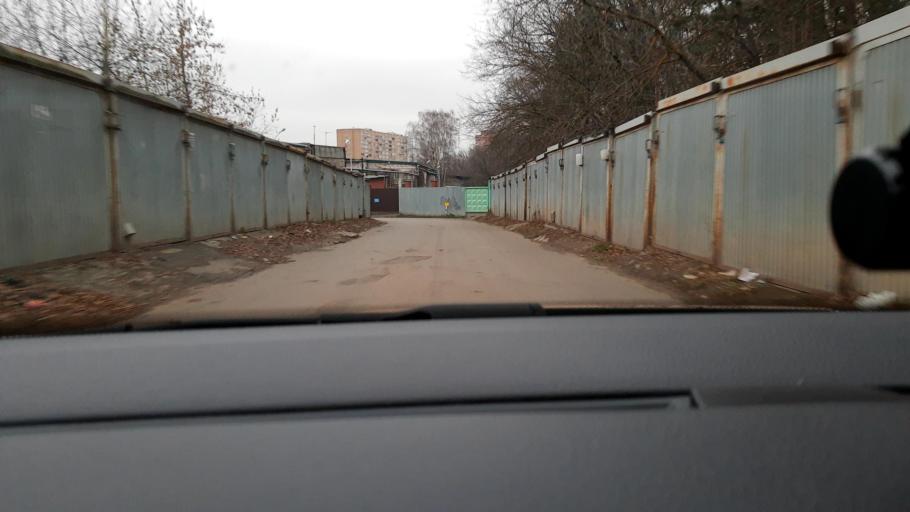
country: RU
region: Moskovskaya
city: Koptevo
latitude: 55.8182
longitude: 37.5365
